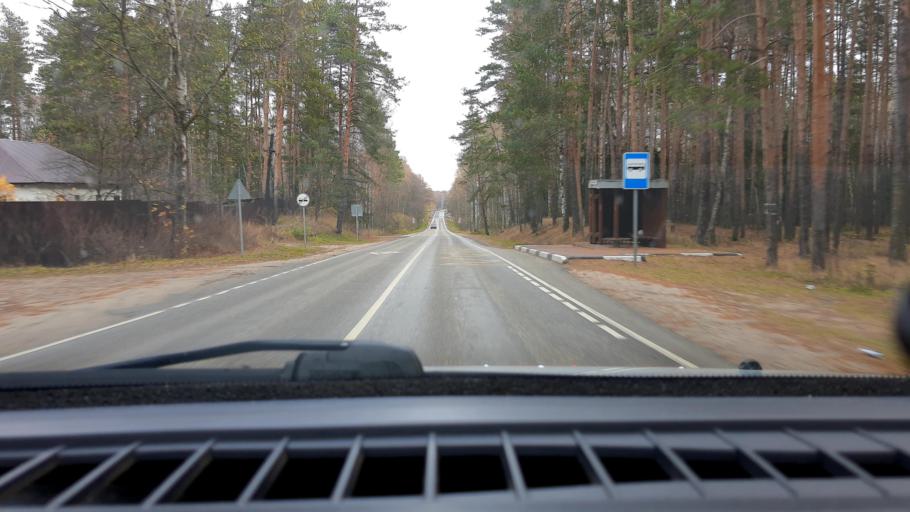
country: RU
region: Nizjnij Novgorod
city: Afonino
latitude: 56.1849
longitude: 44.1104
